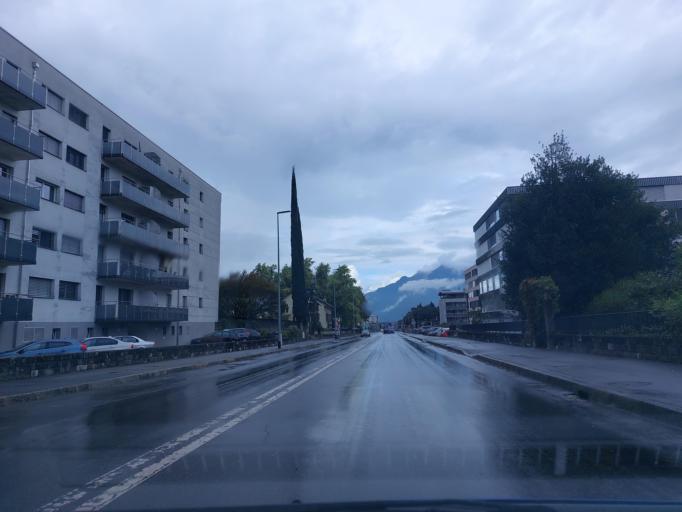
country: CH
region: Valais
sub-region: Monthey District
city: Collombey
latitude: 46.2559
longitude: 6.9458
